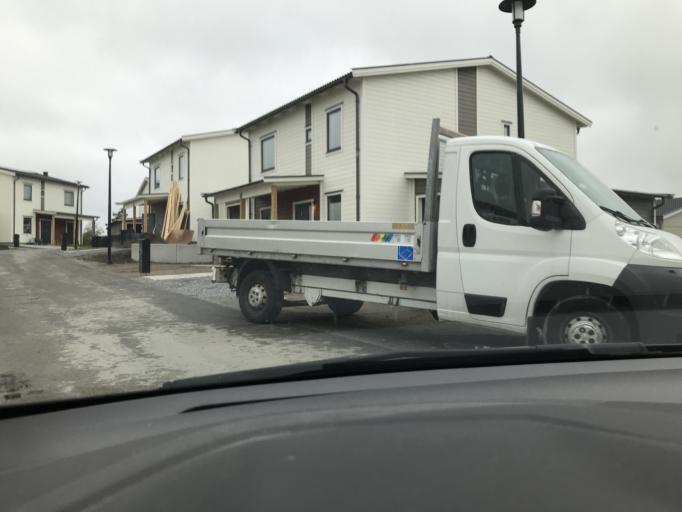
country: SE
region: Stockholm
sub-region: Botkyrka Kommun
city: Tumba
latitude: 59.2086
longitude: 17.8435
